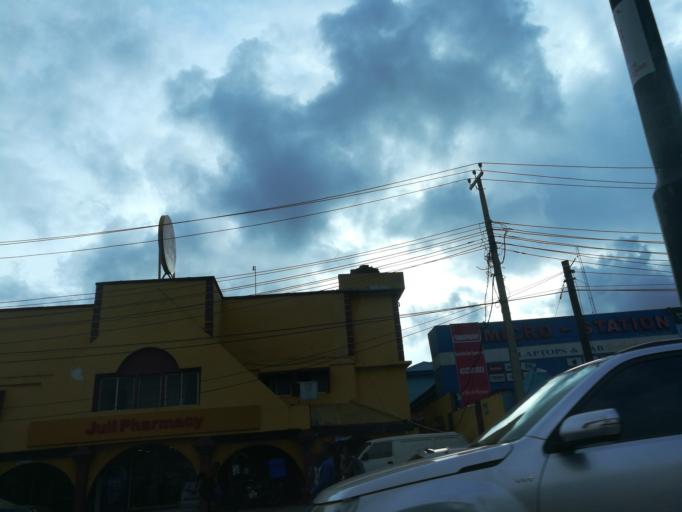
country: NG
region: Lagos
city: Ikeja
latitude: 6.5946
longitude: 3.3417
